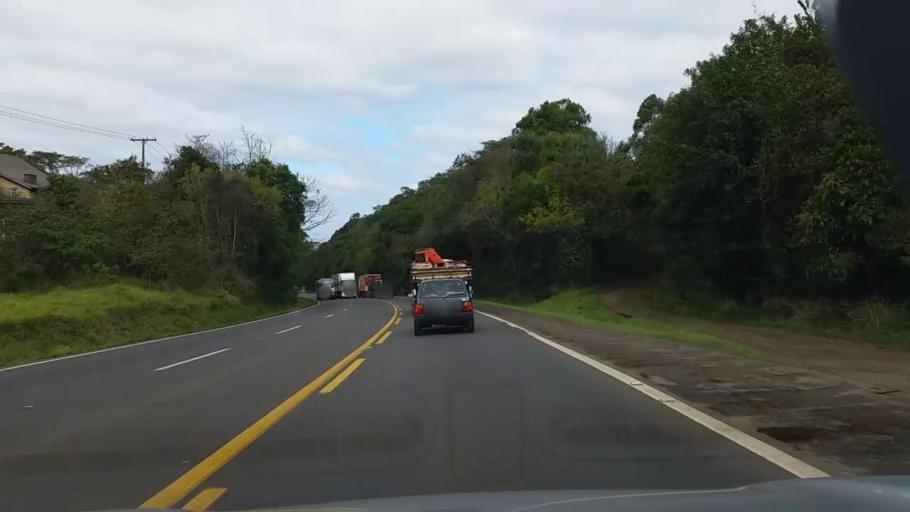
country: BR
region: Rio Grande do Sul
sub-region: Arroio Do Meio
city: Arroio do Meio
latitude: -29.3946
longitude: -52.0427
